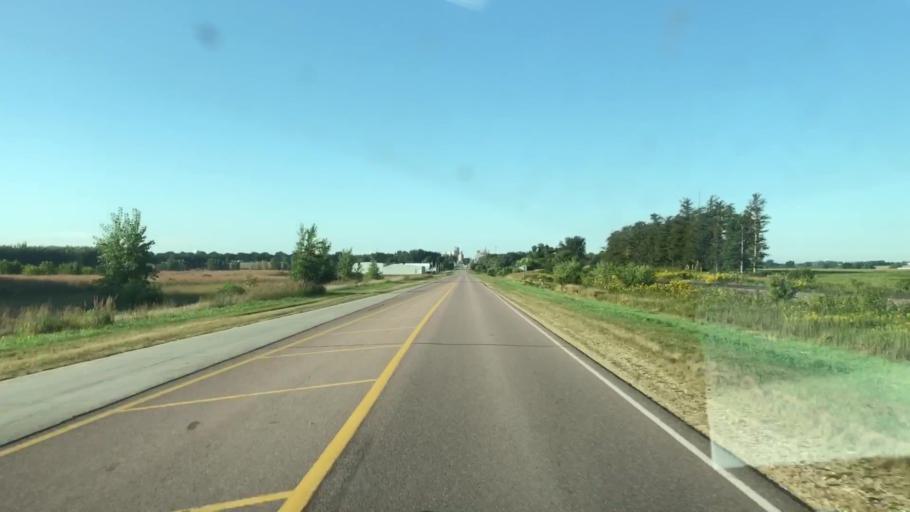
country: US
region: Iowa
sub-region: O'Brien County
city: Sheldon
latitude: 43.2048
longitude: -95.8442
